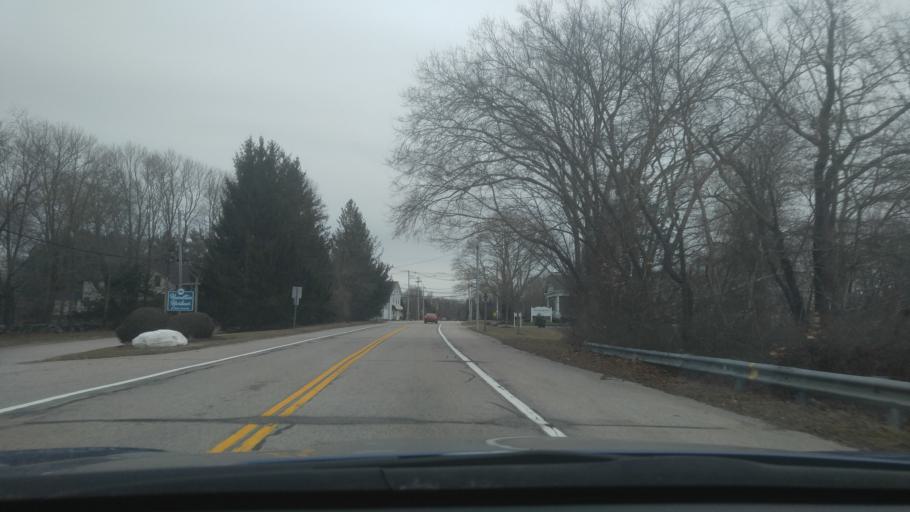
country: US
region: Rhode Island
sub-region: Washington County
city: North Kingstown
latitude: 41.5502
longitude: -71.4409
